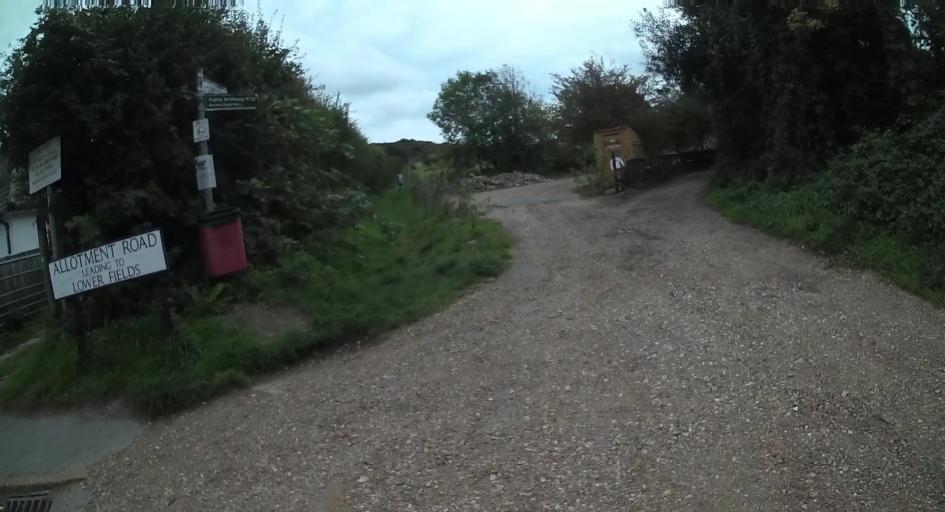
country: GB
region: England
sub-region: Isle of Wight
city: Niton
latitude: 50.5878
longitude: -1.2809
